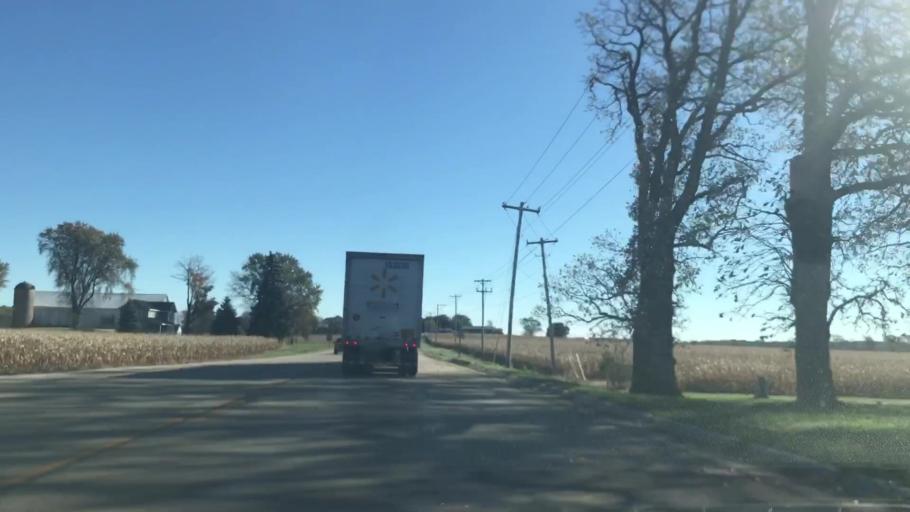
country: US
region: Wisconsin
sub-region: Dodge County
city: Juneau
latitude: 43.4446
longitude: -88.7504
